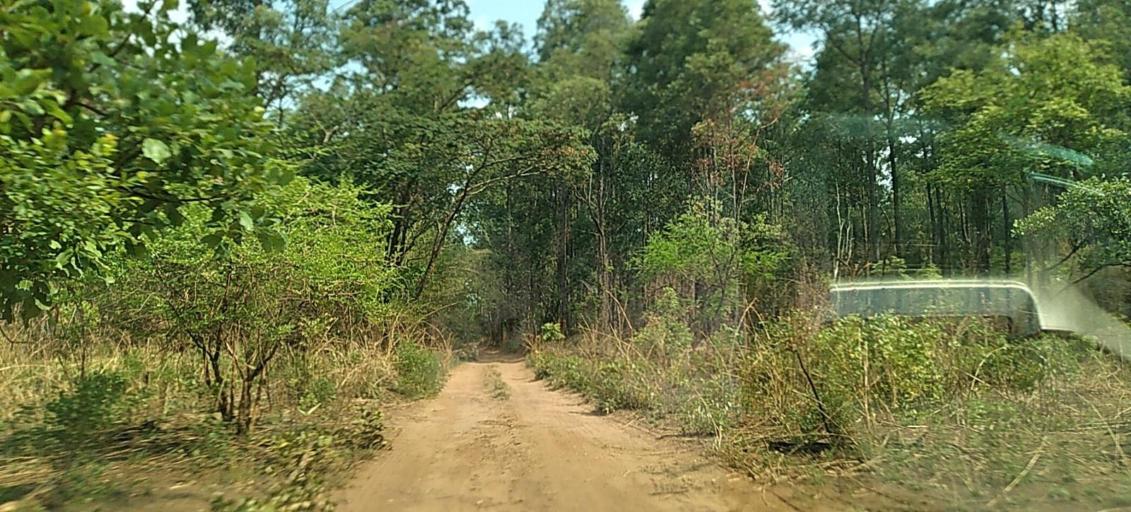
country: ZM
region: Copperbelt
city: Chingola
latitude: -12.7380
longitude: 27.7588
